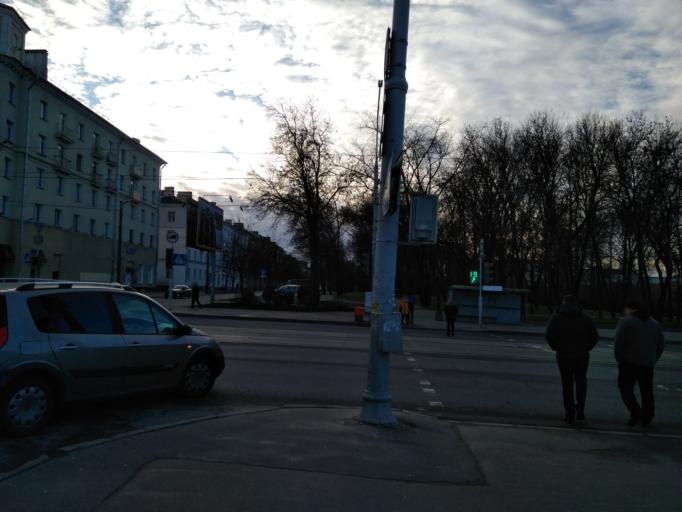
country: BY
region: Minsk
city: Minsk
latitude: 53.9018
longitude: 27.6017
